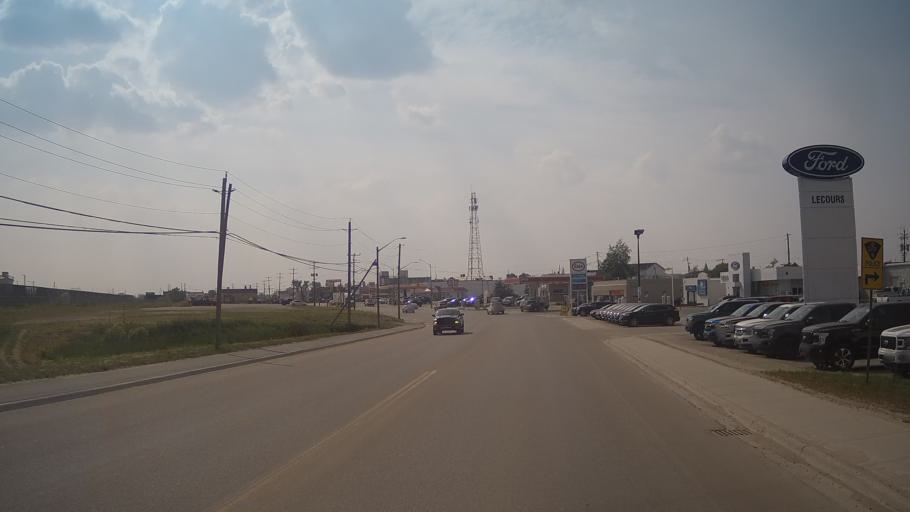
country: CA
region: Ontario
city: Kapuskasing
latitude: 49.4127
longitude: -82.4170
